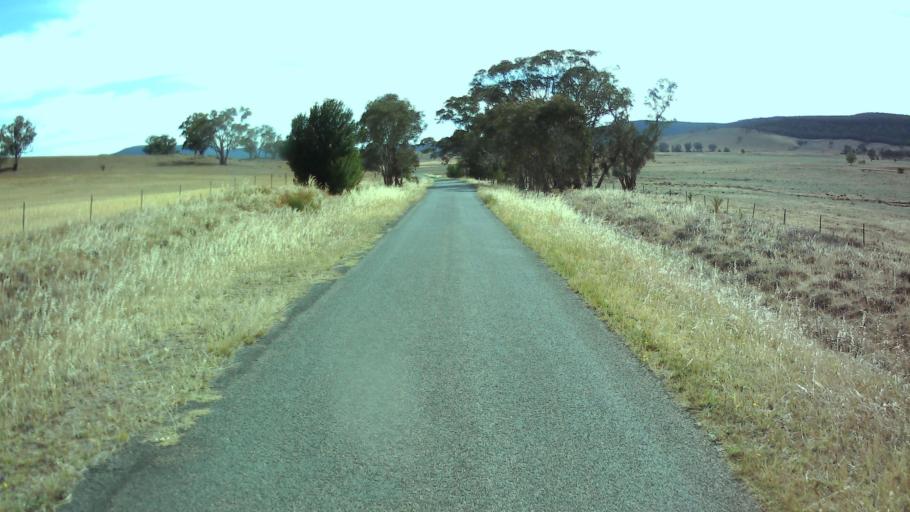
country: AU
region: New South Wales
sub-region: Weddin
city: Grenfell
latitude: -33.8269
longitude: 148.2852
